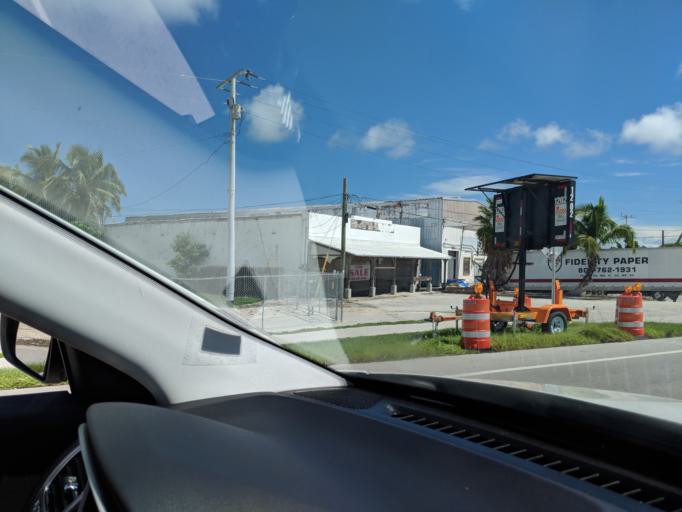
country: US
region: Florida
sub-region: Monroe County
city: Marathon
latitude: 24.7081
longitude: -81.1134
